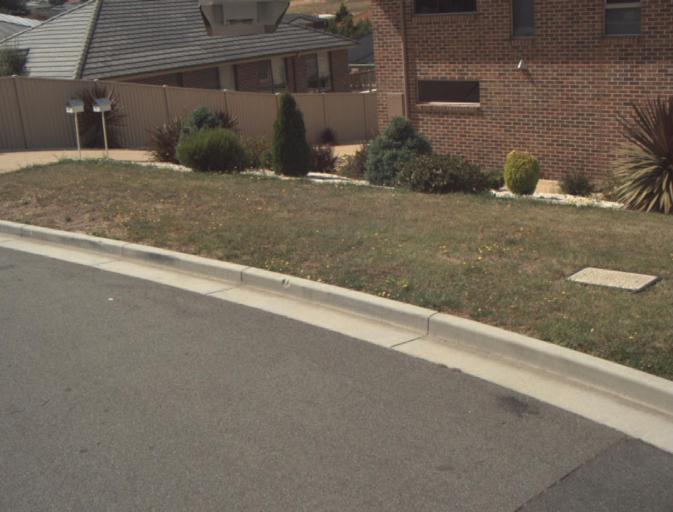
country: AU
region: Tasmania
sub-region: Launceston
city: Mayfield
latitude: -41.3862
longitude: 147.1097
